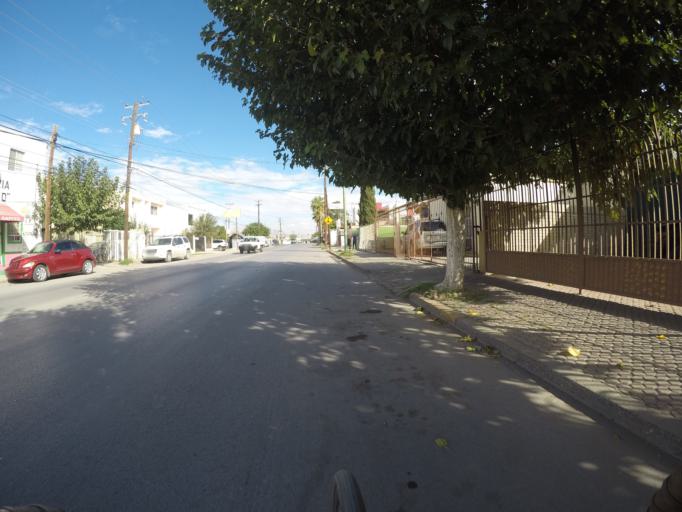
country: MX
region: Chihuahua
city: Ciudad Juarez
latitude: 31.7408
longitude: -106.4334
